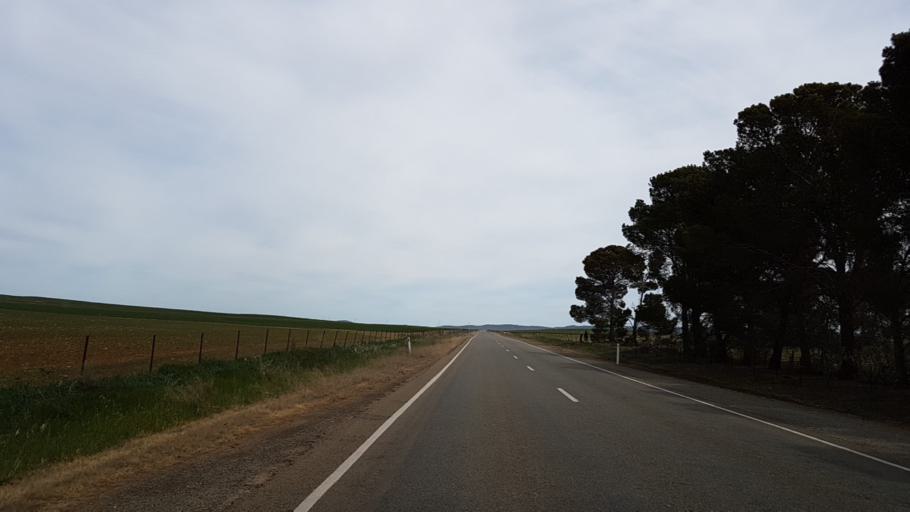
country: AU
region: South Australia
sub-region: Peterborough
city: Peterborough
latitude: -33.0201
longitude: 138.6862
